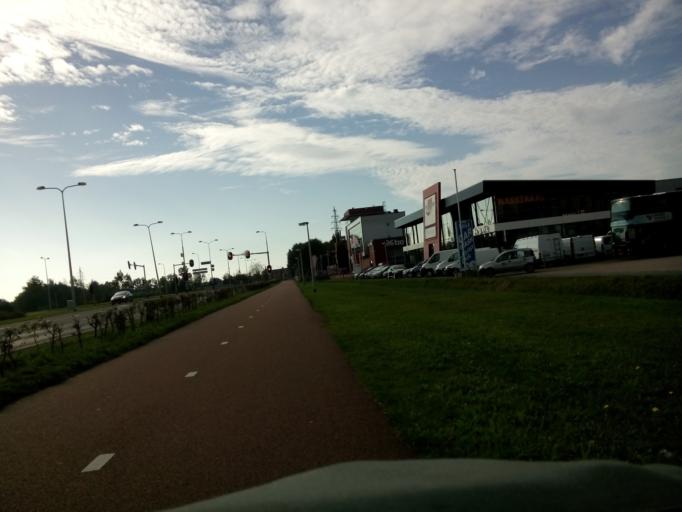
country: NL
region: Drenthe
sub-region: Gemeente Assen
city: Assen
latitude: 53.0241
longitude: 6.5716
